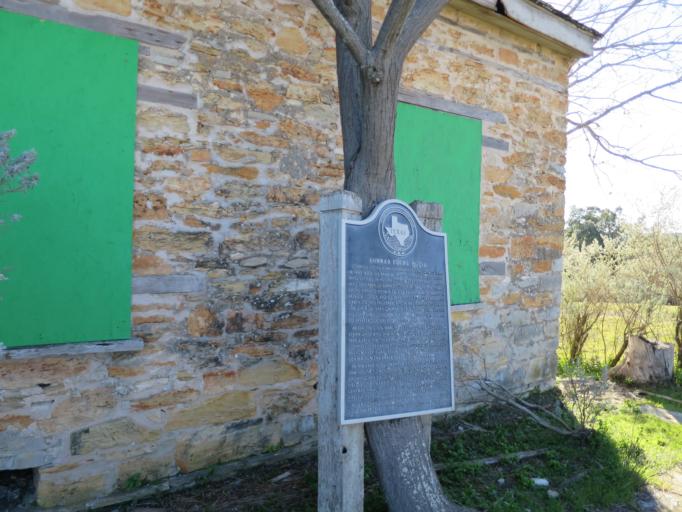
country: US
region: Texas
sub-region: Llano County
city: Horseshoe Bay
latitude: 30.5332
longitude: -98.3275
